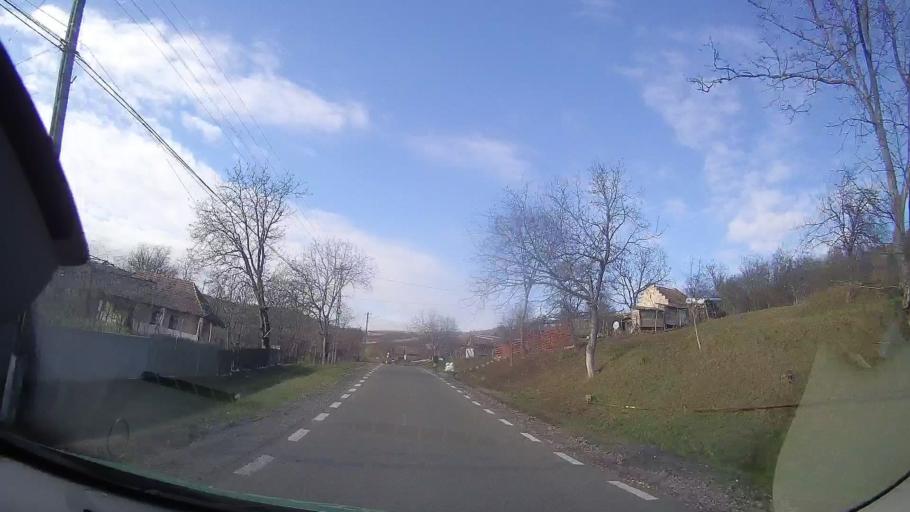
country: RO
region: Mures
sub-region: Comuna Papiu Ilarian
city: Papiu Ilarian
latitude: 46.5586
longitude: 24.1871
